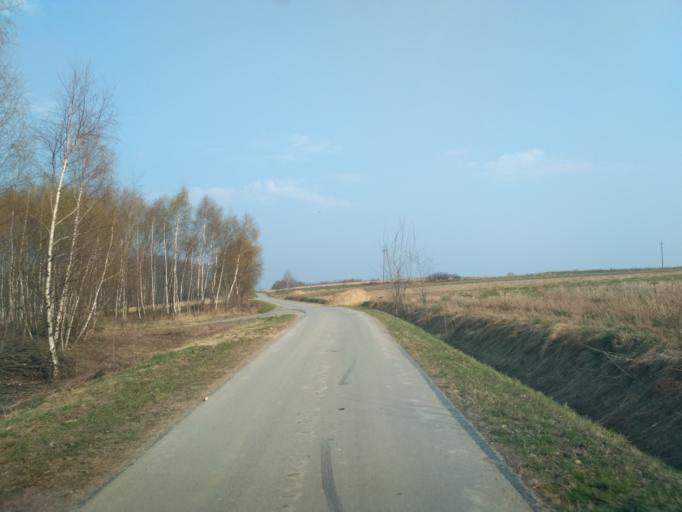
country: PL
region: Subcarpathian Voivodeship
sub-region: Powiat ropczycko-sedziszowski
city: Wielopole Skrzynskie
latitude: 49.8978
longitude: 21.6114
